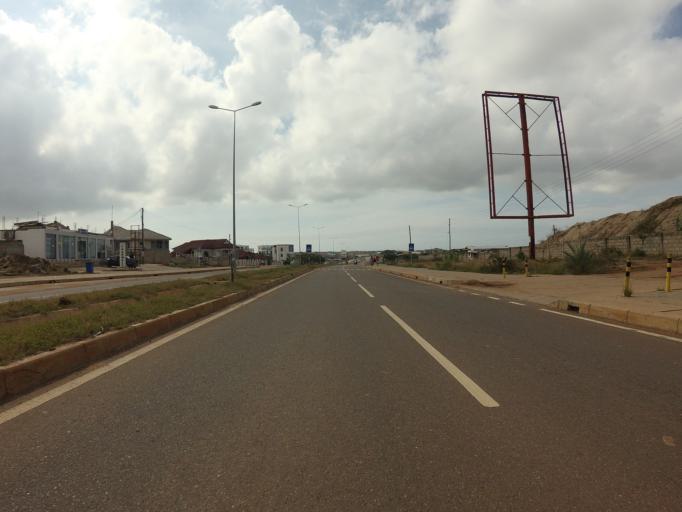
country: GH
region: Greater Accra
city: Teshi Old Town
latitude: 5.6002
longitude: -0.1366
